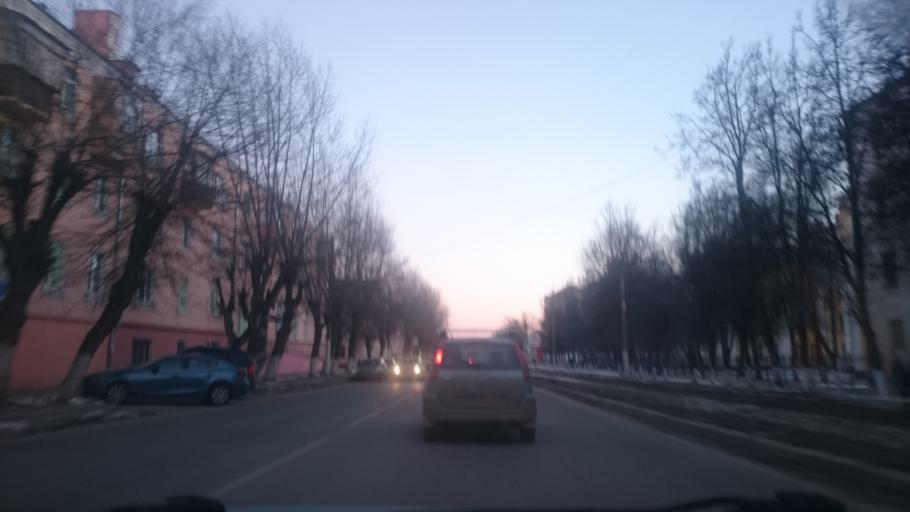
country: RU
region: Tula
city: Tula
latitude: 54.1866
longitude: 37.6954
